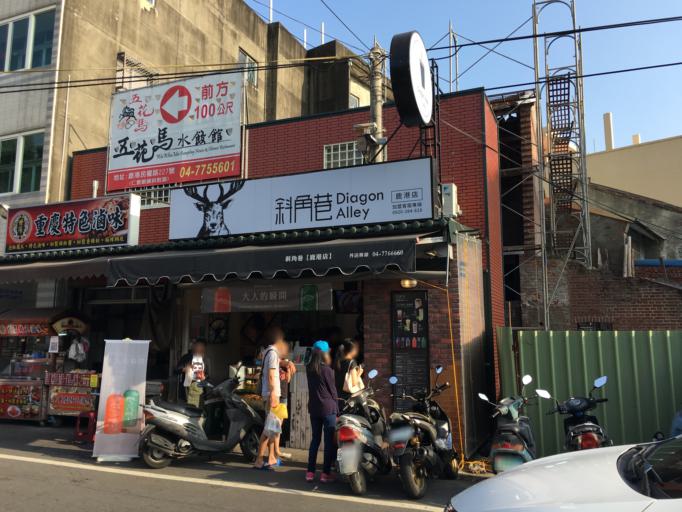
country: TW
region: Taiwan
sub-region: Changhua
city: Chang-hua
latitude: 24.0557
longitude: 120.4331
